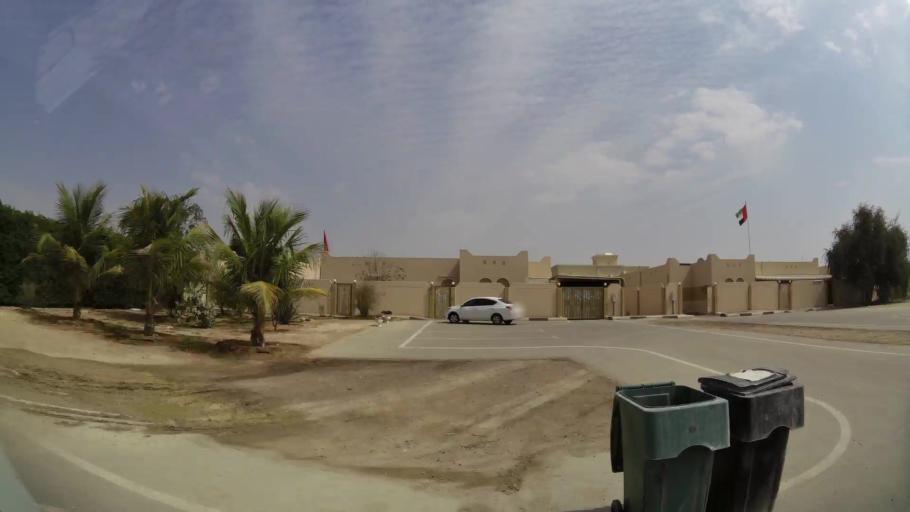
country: AE
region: Abu Dhabi
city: Abu Dhabi
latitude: 24.5298
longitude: 54.6804
